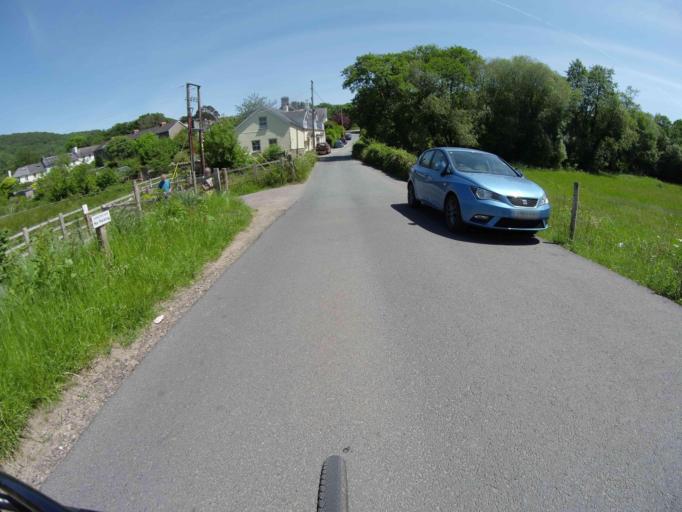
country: GB
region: England
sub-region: Devon
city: Bovey Tracey
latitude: 50.6202
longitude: -3.7153
